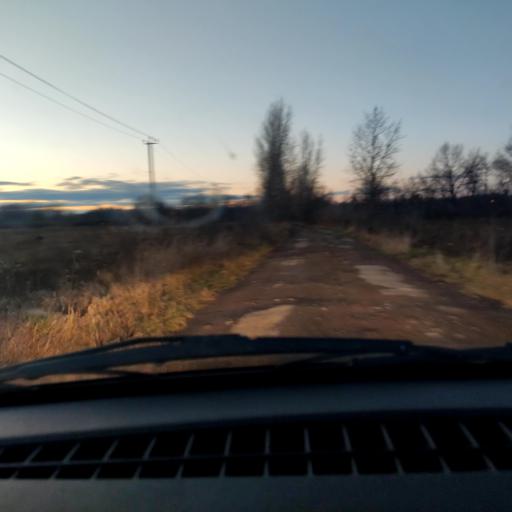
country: RU
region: Bashkortostan
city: Ufa
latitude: 54.6526
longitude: 55.8911
